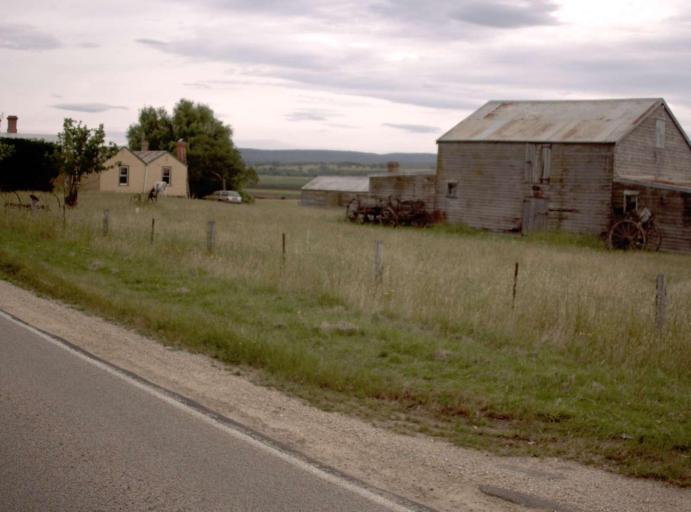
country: AU
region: Victoria
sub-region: East Gippsland
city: Bairnsdale
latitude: -37.8154
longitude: 147.4912
